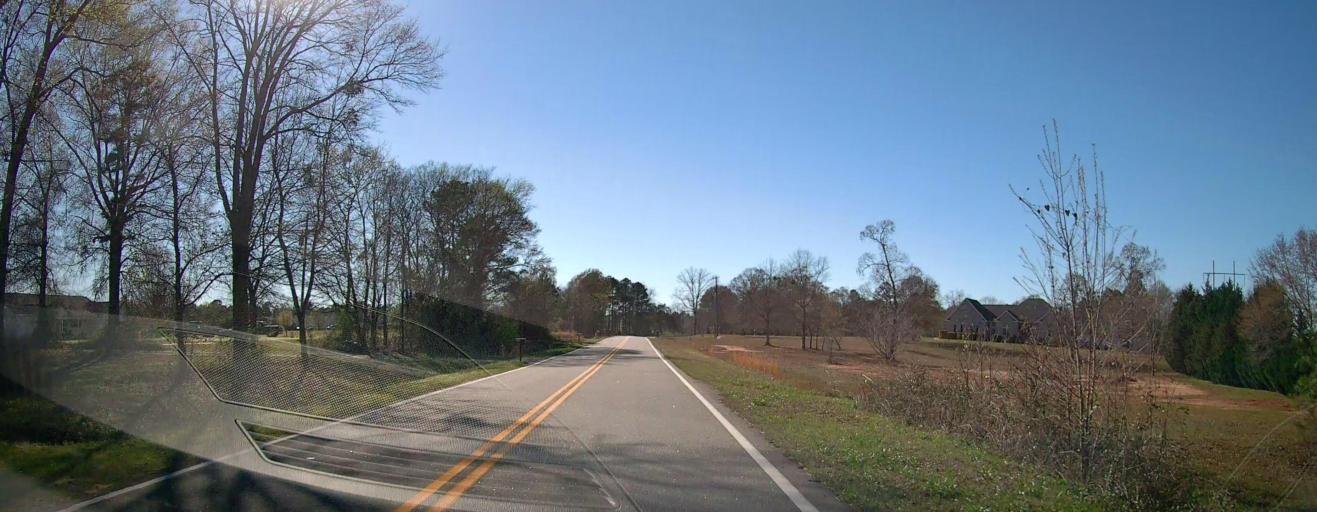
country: US
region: Georgia
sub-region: Peach County
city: Byron
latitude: 32.6734
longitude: -83.8254
